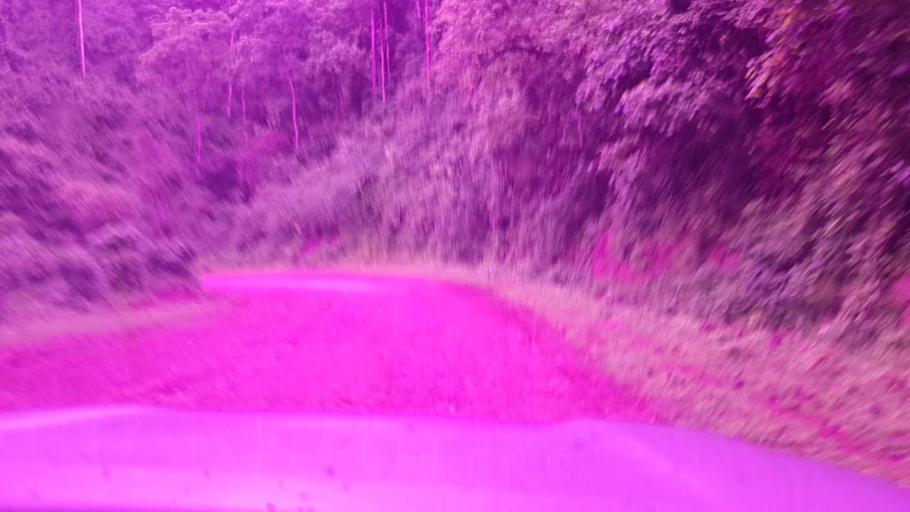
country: ET
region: Southern Nations, Nationalities, and People's Region
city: Bonga
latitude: 7.5087
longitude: 36.0653
